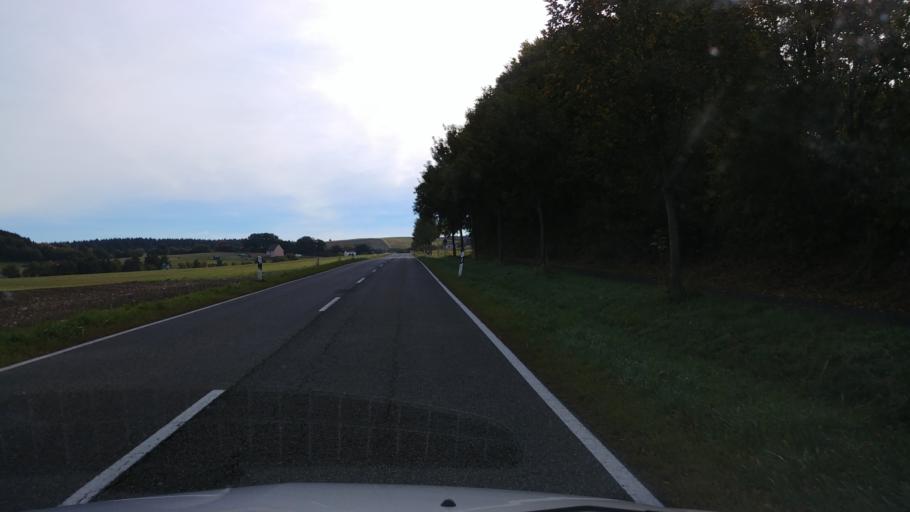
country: DE
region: Hesse
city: Burg Hohenstein
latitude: 50.1916
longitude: 8.1131
